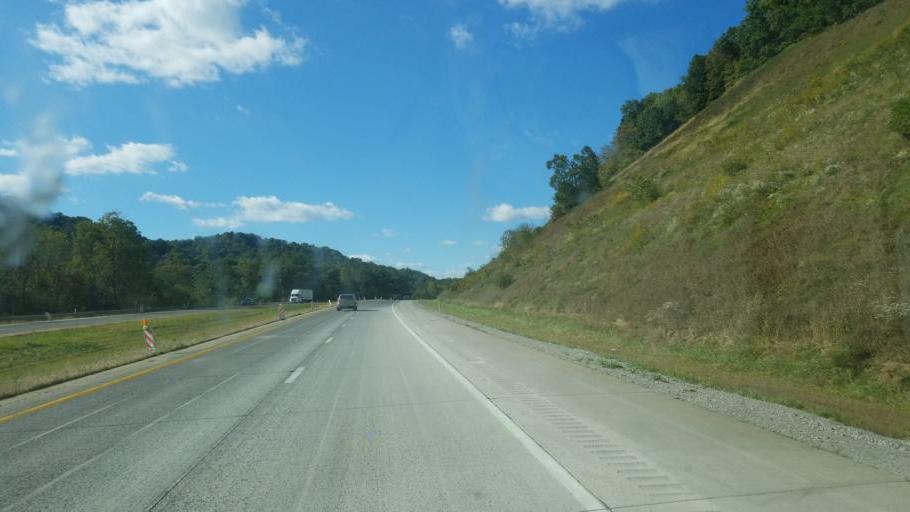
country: US
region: West Virginia
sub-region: Monongalia County
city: Star City
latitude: 39.7480
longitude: -80.0718
